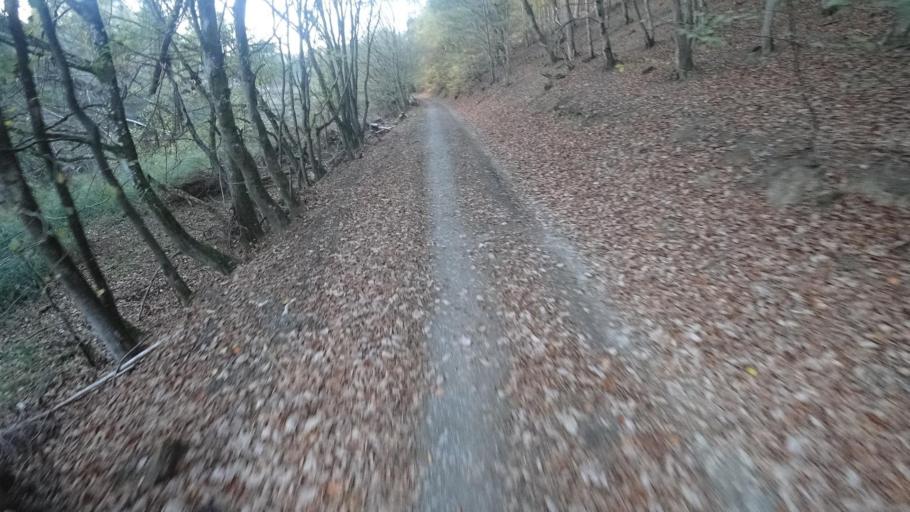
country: DE
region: Rheinland-Pfalz
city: Berg
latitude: 50.5321
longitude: 6.9575
